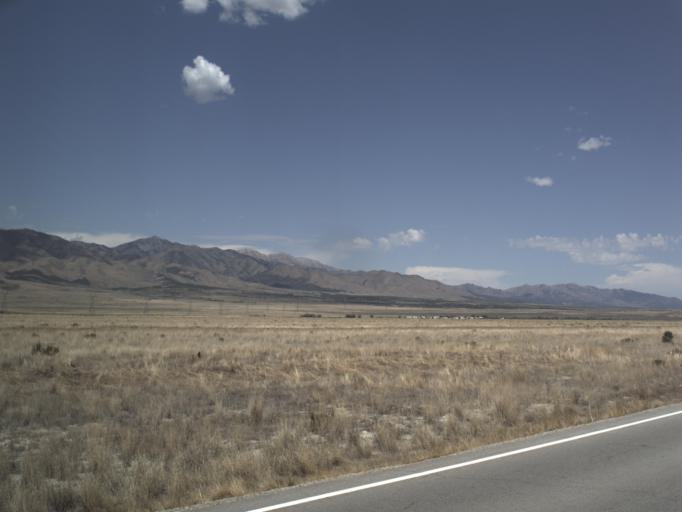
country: US
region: Utah
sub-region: Tooele County
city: Tooele
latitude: 40.3560
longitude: -112.4132
